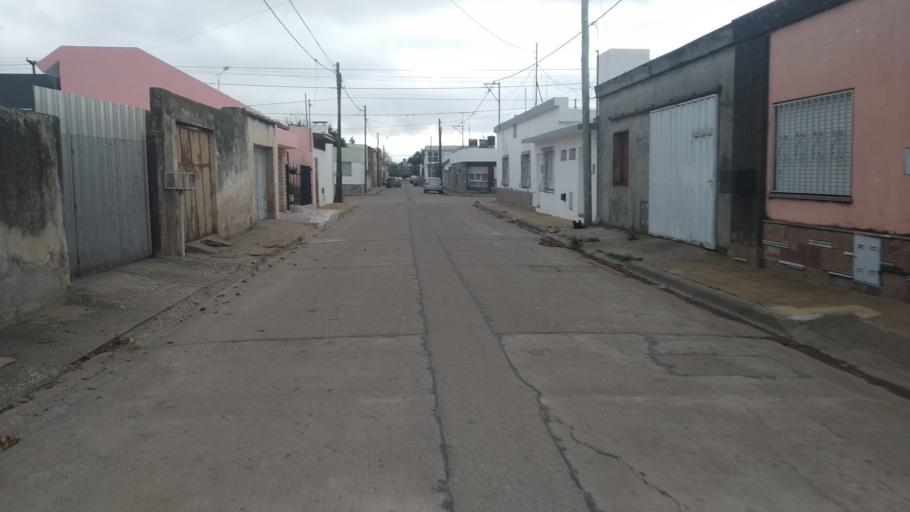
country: AR
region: Cordoba
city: Leones
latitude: -32.6611
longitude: -62.3021
